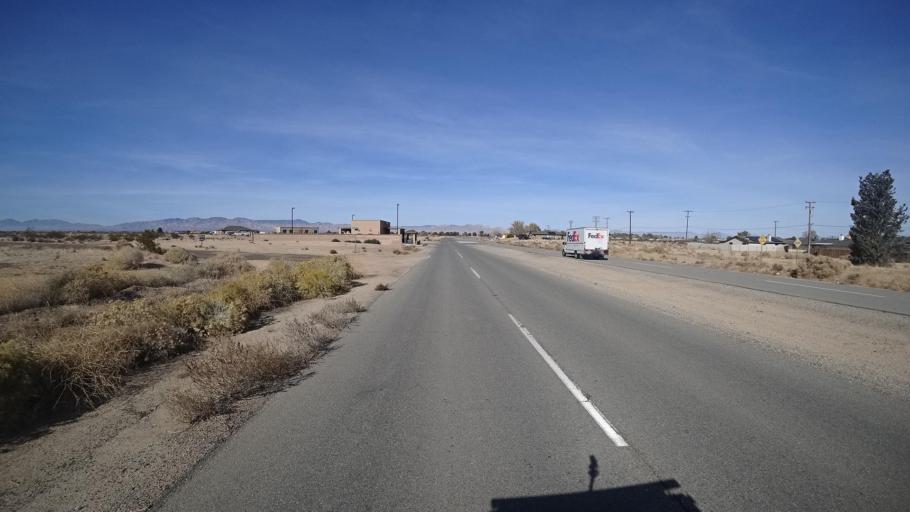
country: US
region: California
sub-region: Kern County
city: California City
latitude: 35.1185
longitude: -117.9381
